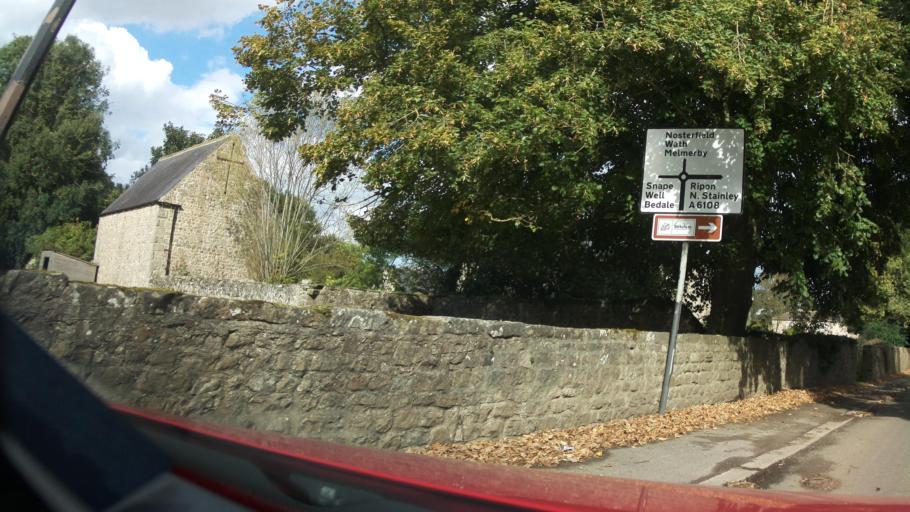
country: GB
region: England
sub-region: North Yorkshire
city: Bedale
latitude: 54.2042
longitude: -1.5916
